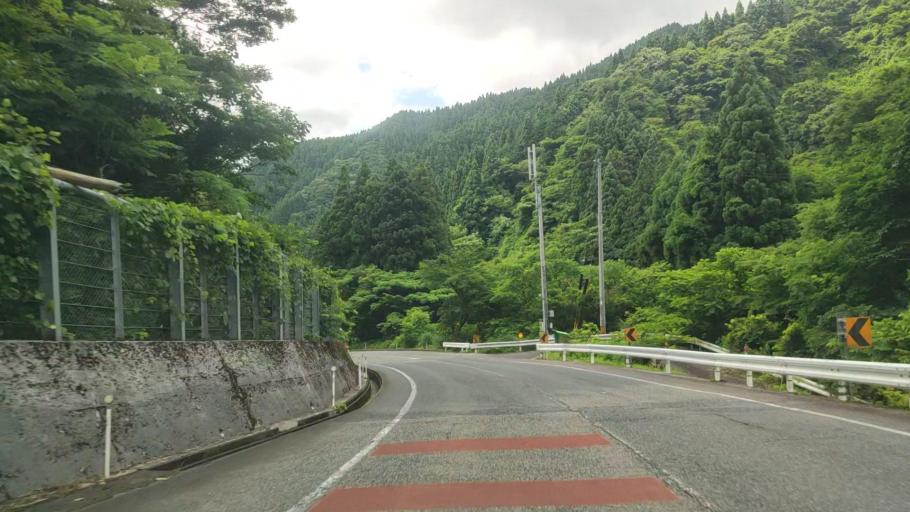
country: JP
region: Tottori
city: Yonago
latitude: 35.2561
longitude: 133.4368
